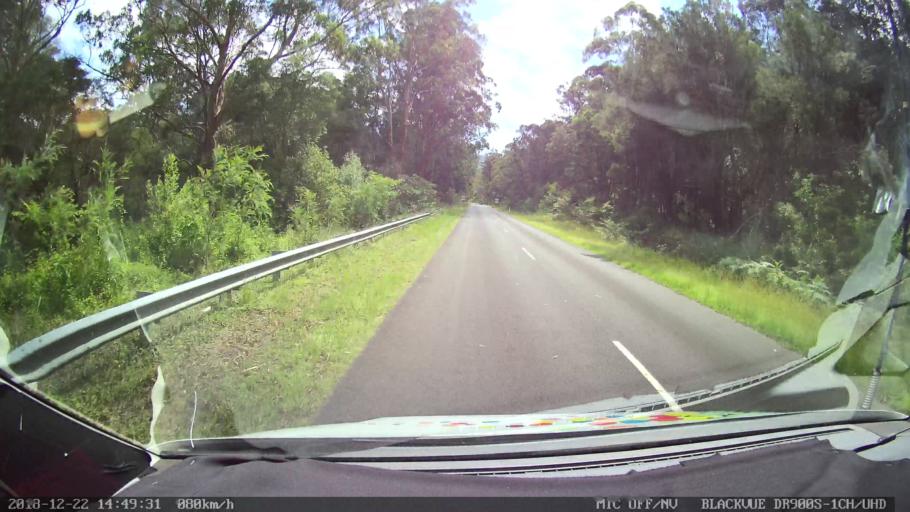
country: AU
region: New South Wales
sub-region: Bellingen
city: Dorrigo
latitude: -30.1890
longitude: 152.5467
